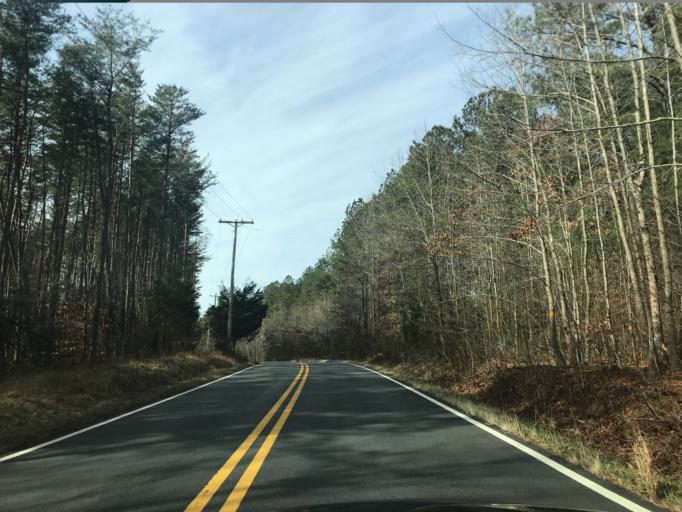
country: US
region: Maryland
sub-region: Charles County
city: Indian Head
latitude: 38.5002
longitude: -77.1897
